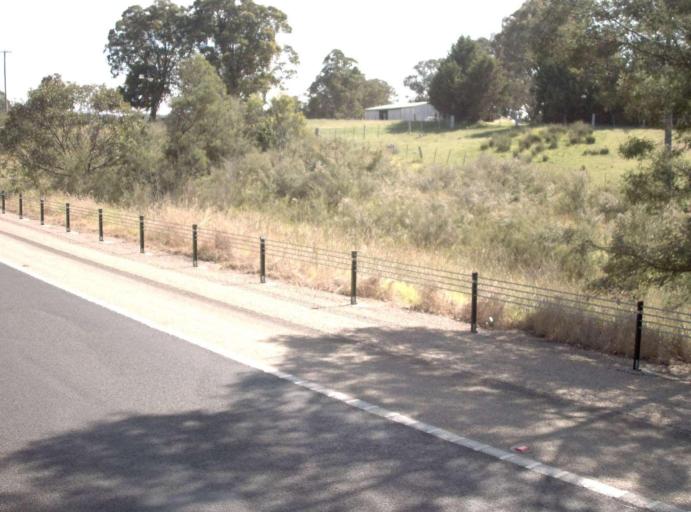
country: AU
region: Victoria
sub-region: East Gippsland
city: Bairnsdale
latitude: -37.7148
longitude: 147.8056
